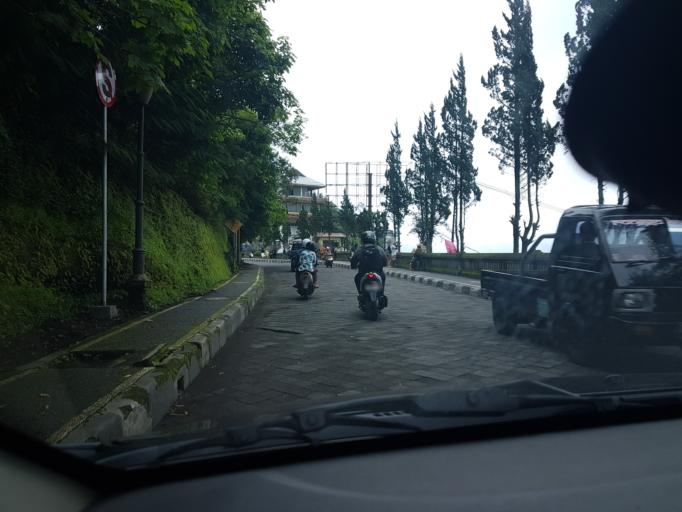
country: ID
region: Bali
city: Banjar Kedisan
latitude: -8.2827
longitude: 115.3639
